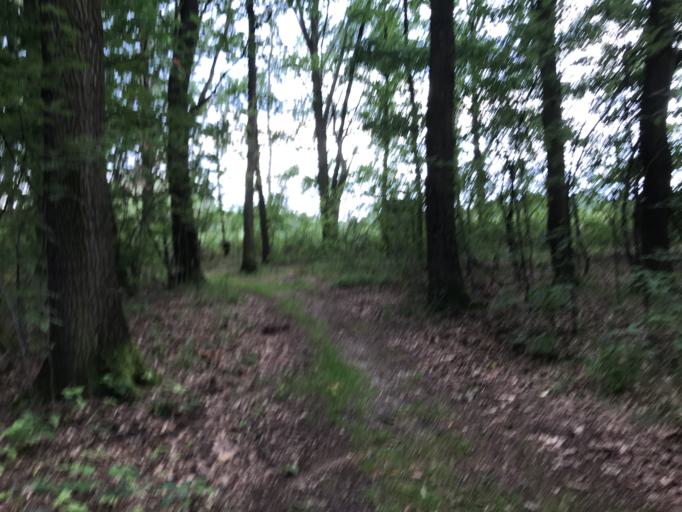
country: CZ
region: Jihocesky
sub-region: Okres Jindrichuv Hradec
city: Lomnice nad Luznici
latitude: 49.0953
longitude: 14.7152
